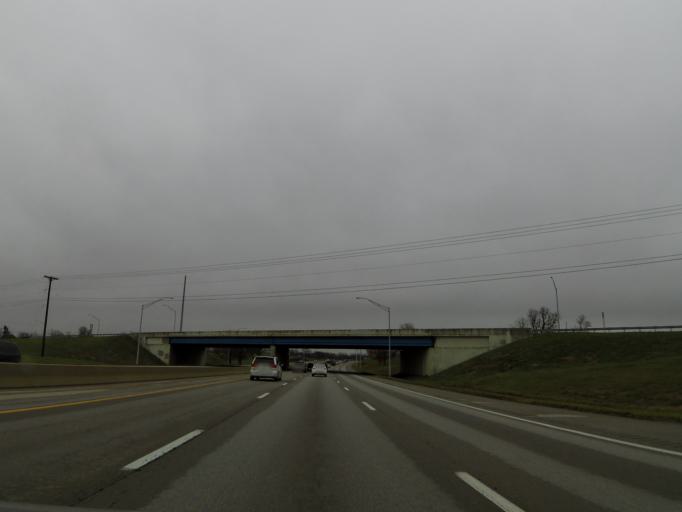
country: US
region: Kentucky
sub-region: Scott County
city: Georgetown
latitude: 38.1490
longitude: -84.5309
